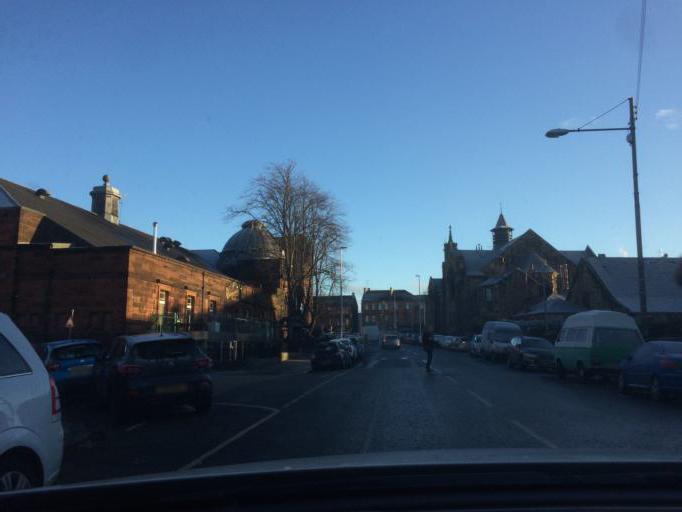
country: GB
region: Scotland
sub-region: East Renfrewshire
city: Giffnock
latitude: 55.8313
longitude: -4.2828
